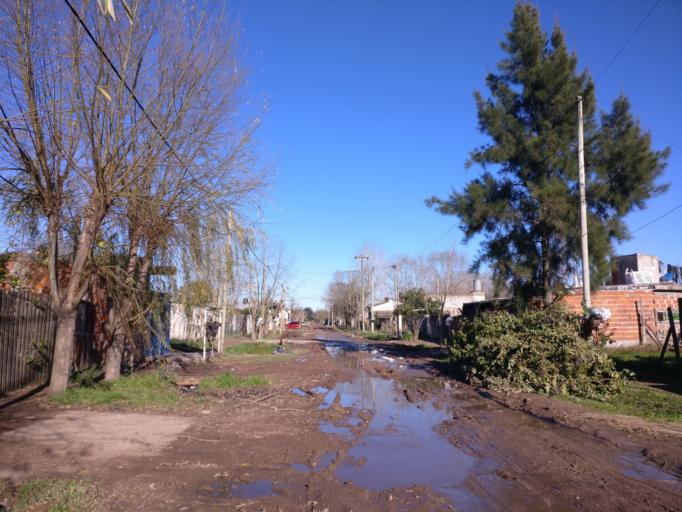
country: AR
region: Buenos Aires
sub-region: Partido de Ezeiza
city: Ezeiza
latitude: -34.9371
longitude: -58.6069
